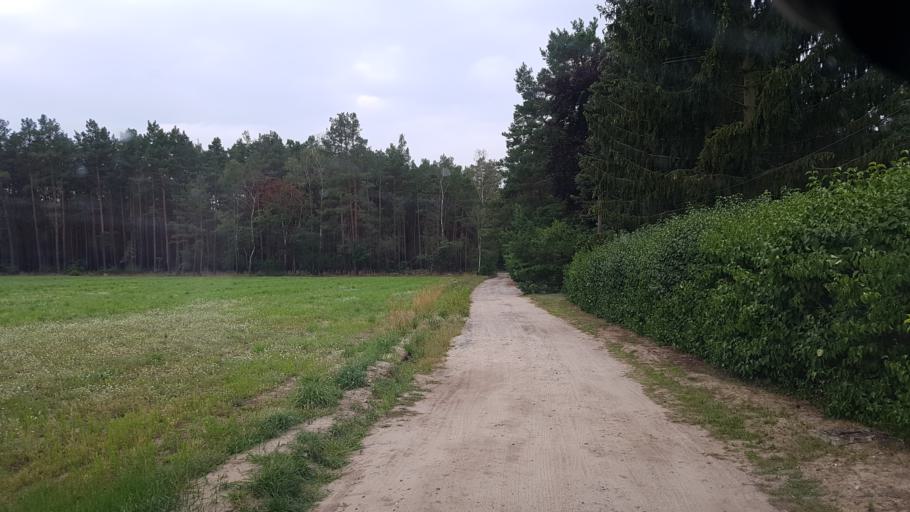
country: DE
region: Brandenburg
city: Gross Koris
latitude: 52.1611
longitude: 13.7006
